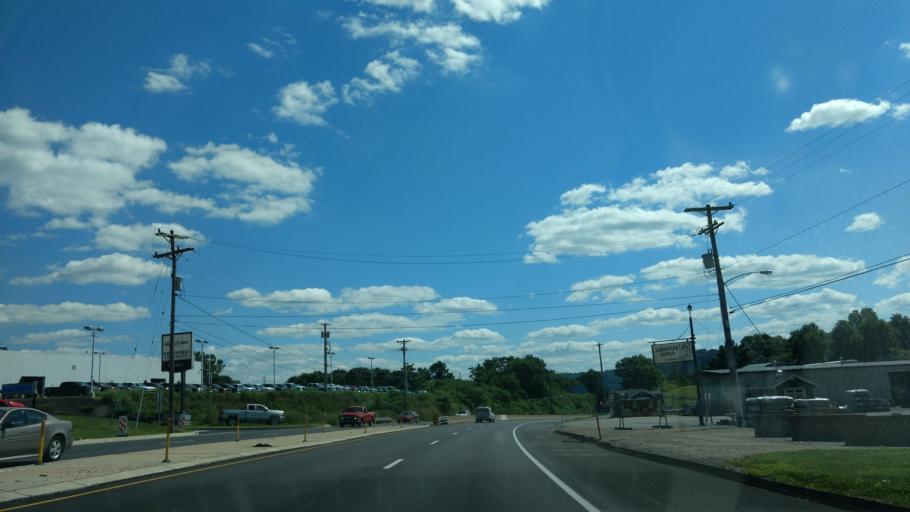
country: US
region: Pennsylvania
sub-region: Beaver County
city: Baden
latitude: 40.6255
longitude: -80.2294
